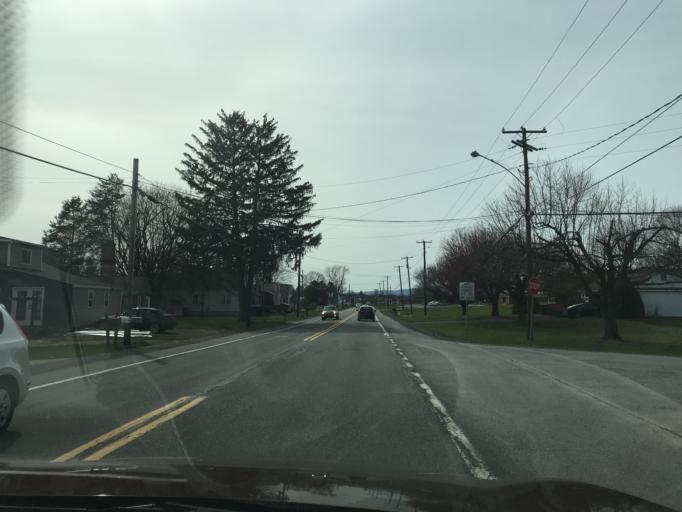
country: US
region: Pennsylvania
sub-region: Union County
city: Lewisburg
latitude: 40.9651
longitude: -76.8450
